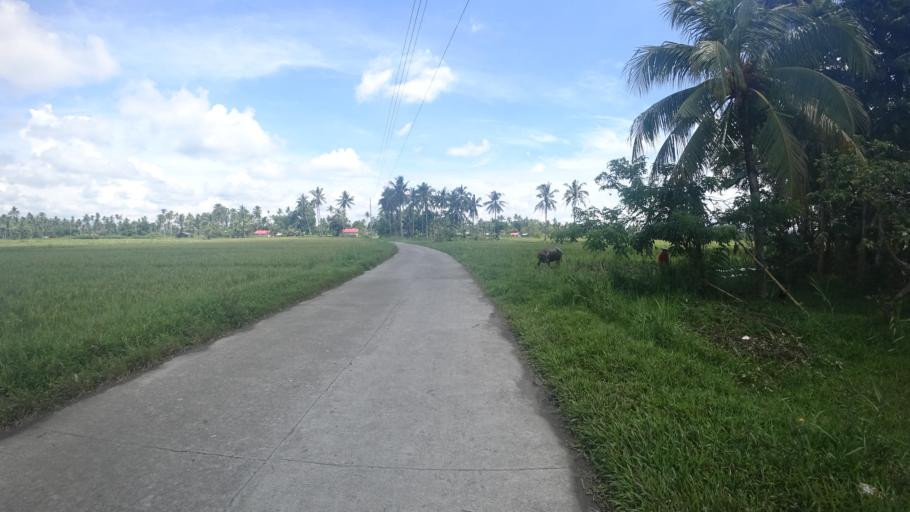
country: PH
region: Eastern Visayas
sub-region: Province of Leyte
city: Alangalang
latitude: 11.2293
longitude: 124.8452
